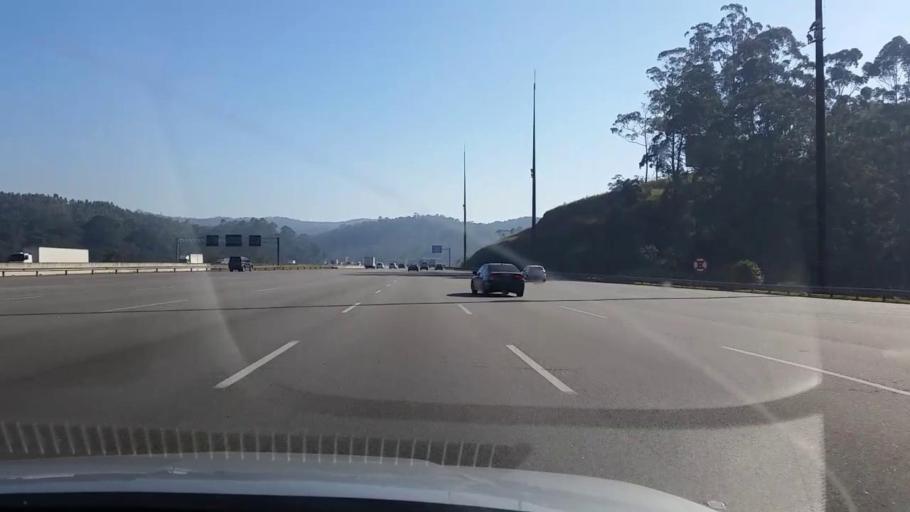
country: BR
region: Sao Paulo
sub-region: Cajamar
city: Cajamar
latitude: -23.3218
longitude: -46.8232
